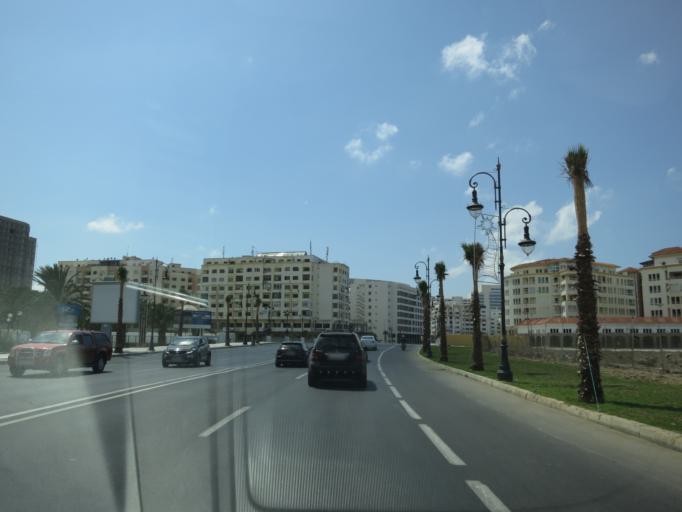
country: MA
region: Tanger-Tetouan
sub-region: Tanger-Assilah
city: Tangier
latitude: 35.7752
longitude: -5.7804
